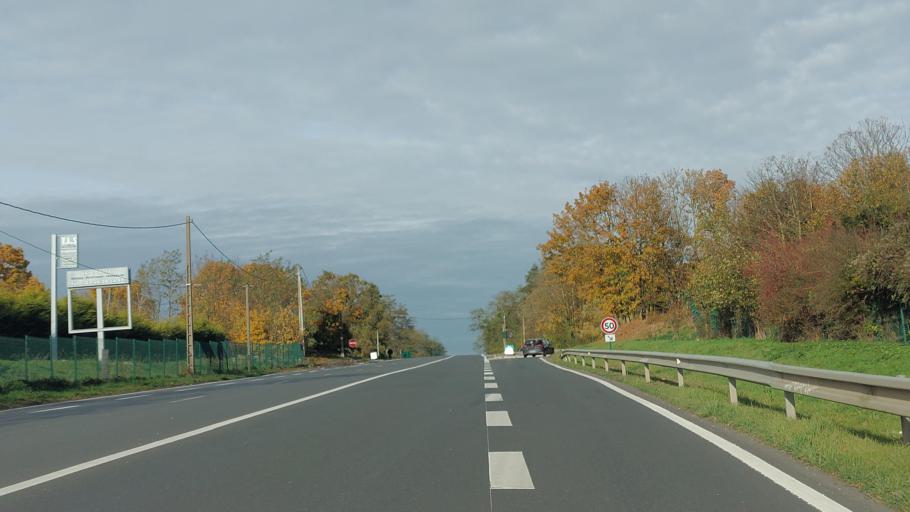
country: FR
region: Ile-de-France
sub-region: Departement du Val-d'Oise
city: Survilliers
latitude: 49.0899
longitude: 2.5304
